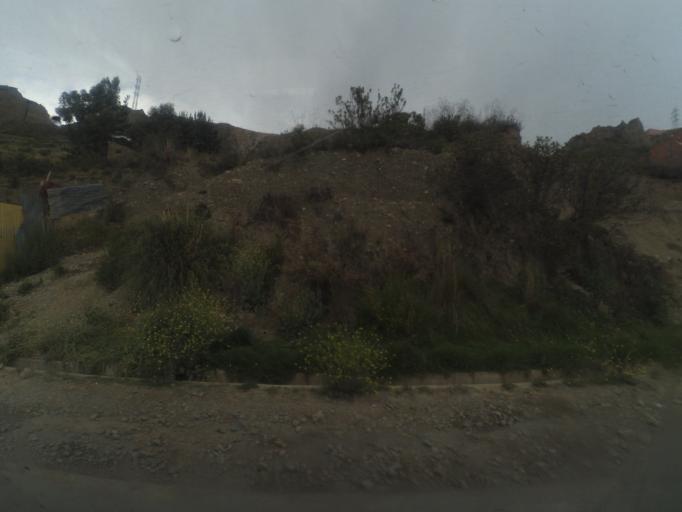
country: BO
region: La Paz
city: La Paz
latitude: -16.5634
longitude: -68.1770
